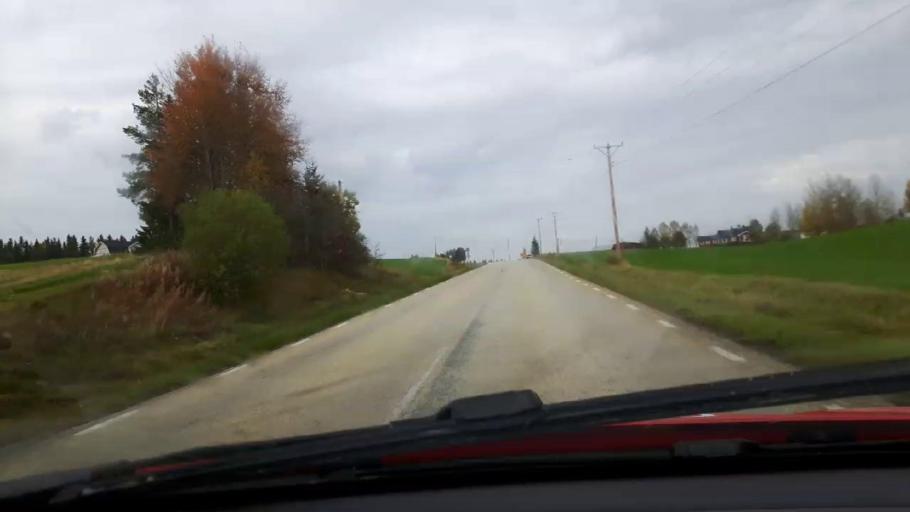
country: SE
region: Jaemtland
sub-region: Bergs Kommun
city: Hoverberg
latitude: 62.9572
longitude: 14.3434
